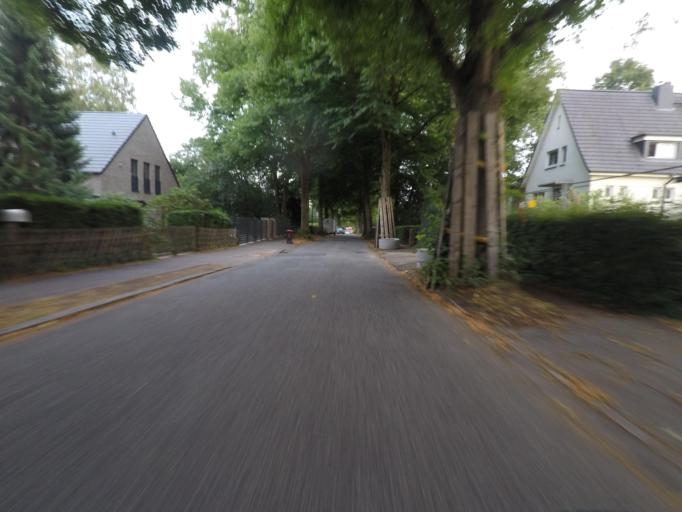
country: DE
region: Hamburg
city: Wellingsbuettel
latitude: 53.6485
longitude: 10.0710
